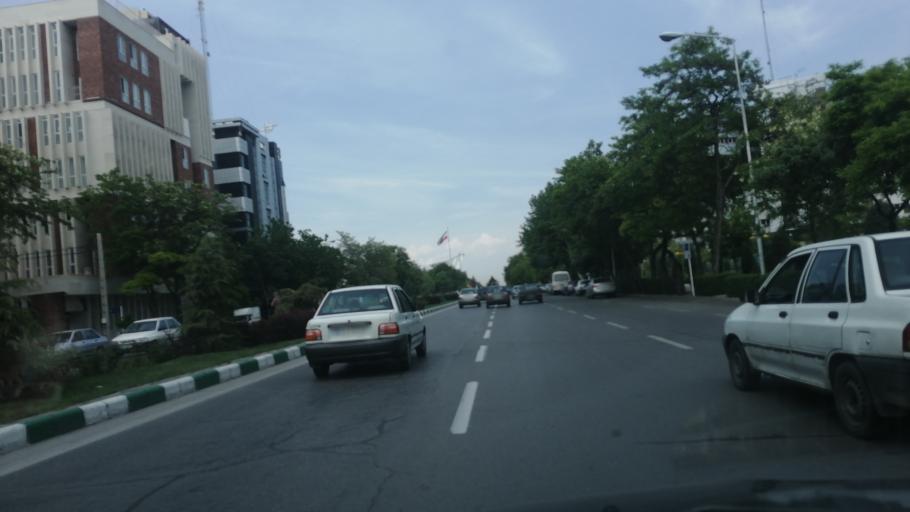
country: IR
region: Razavi Khorasan
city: Mashhad
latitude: 36.3208
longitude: 59.5666
